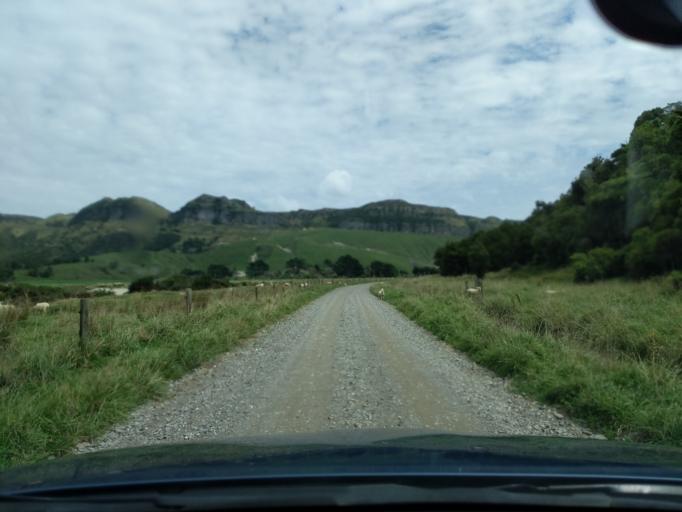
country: NZ
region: Tasman
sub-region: Tasman District
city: Takaka
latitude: -40.6543
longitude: 172.4561
